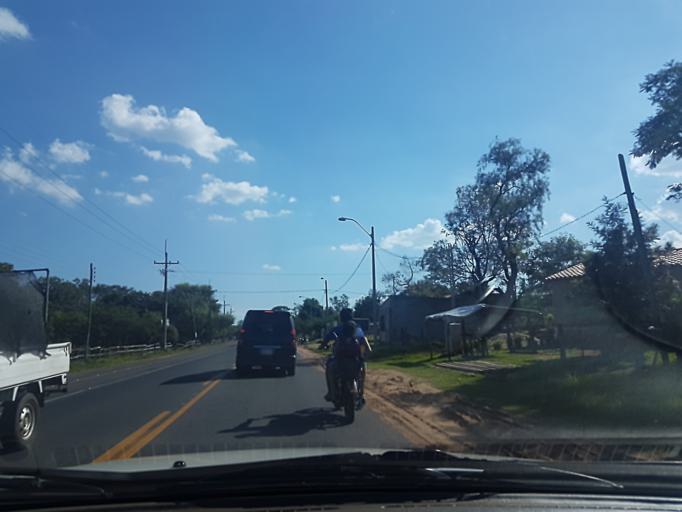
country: PY
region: Central
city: Aregua
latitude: -25.2316
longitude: -57.4191
